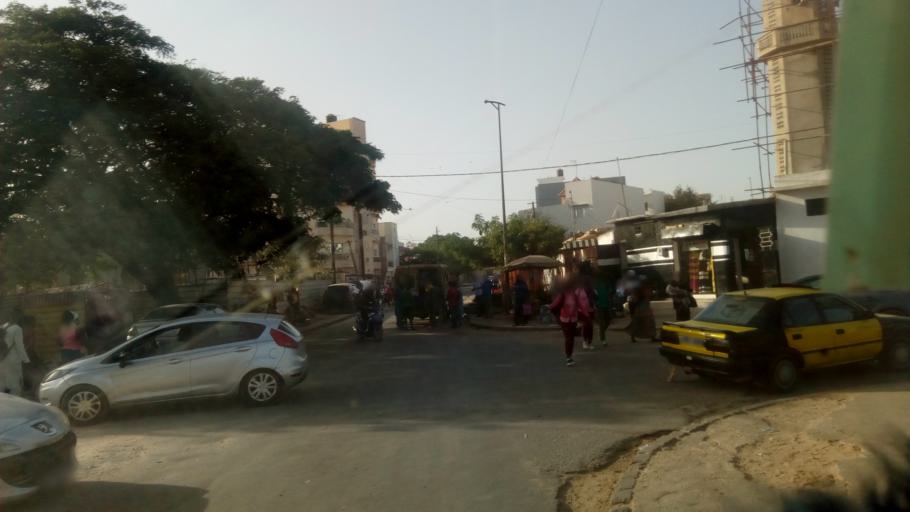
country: SN
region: Dakar
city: Grand Dakar
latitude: 14.7055
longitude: -17.4478
